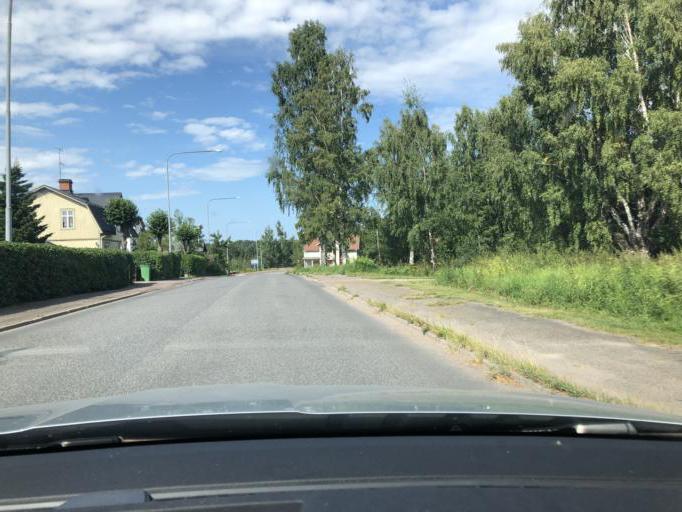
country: SE
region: Dalarna
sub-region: Avesta Kommun
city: Avesta
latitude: 60.1425
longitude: 16.1985
